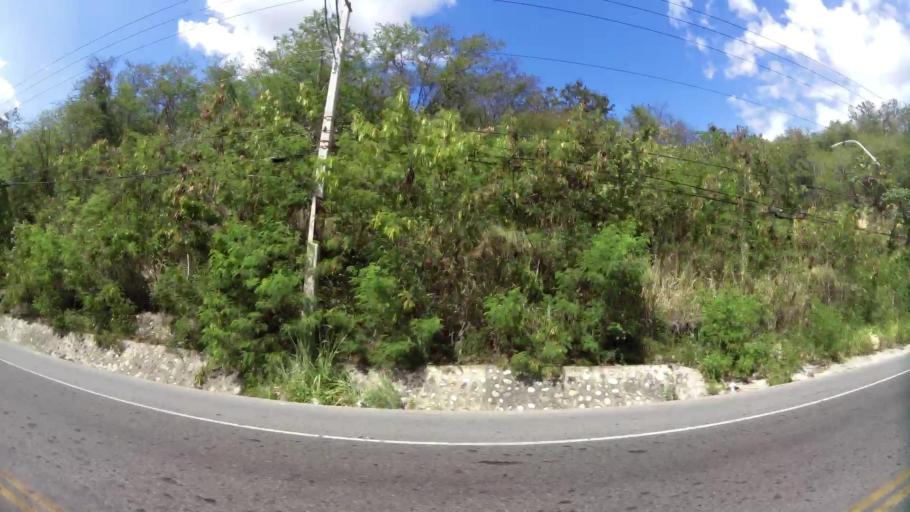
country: DO
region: San Cristobal
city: Bajos de Haina
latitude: 18.4267
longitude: -70.0437
